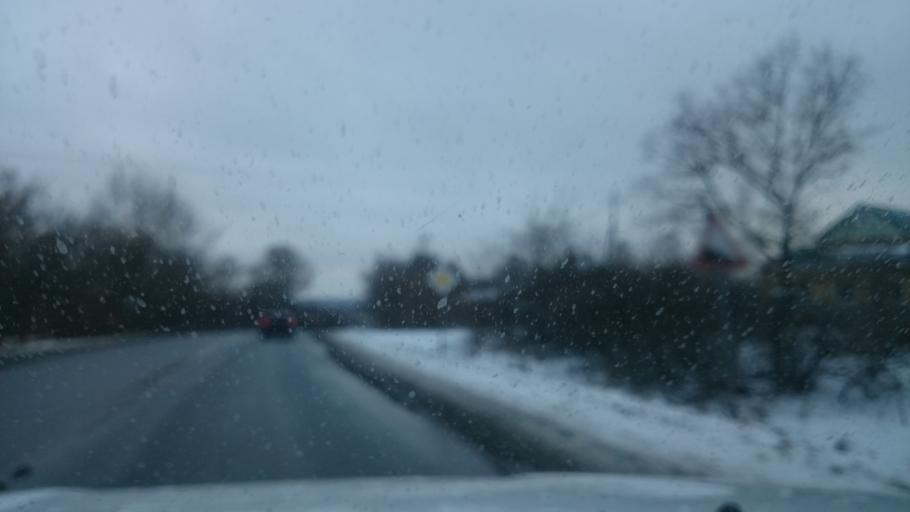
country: RU
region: Tula
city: Mendeleyevskiy
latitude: 54.1309
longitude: 37.5783
